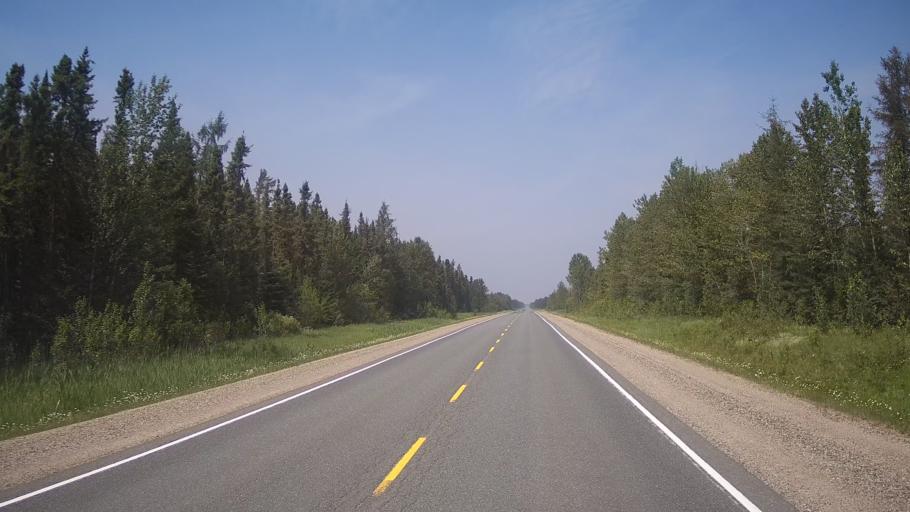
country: CA
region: Ontario
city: Timmins
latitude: 48.8252
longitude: -81.3712
